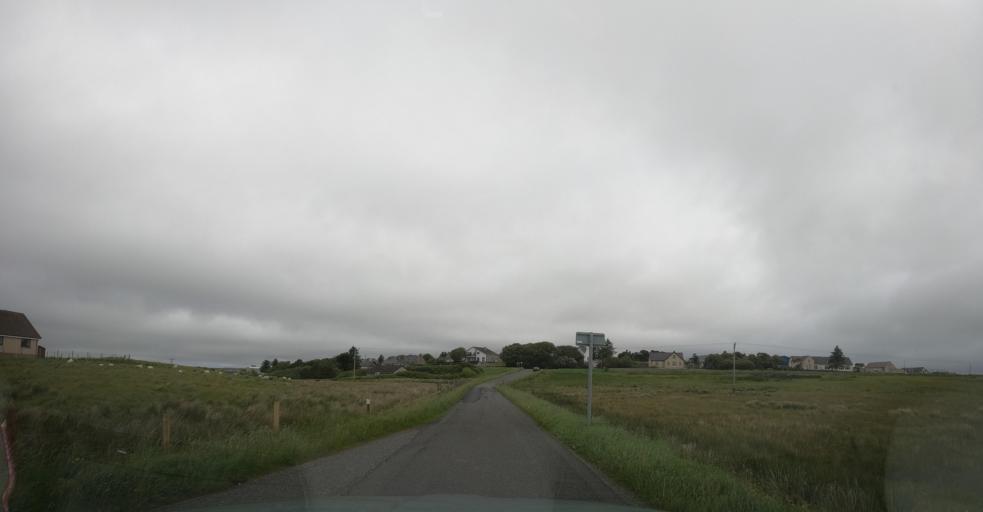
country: GB
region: Scotland
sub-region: Eilean Siar
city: Stornoway
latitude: 58.2022
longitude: -6.3501
